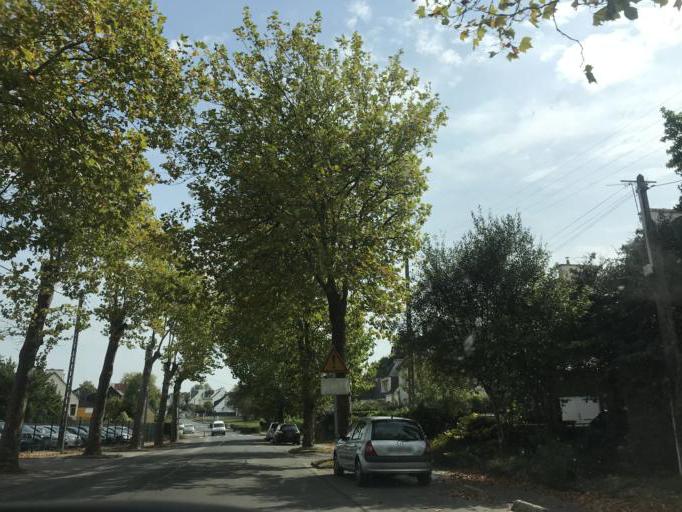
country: FR
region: Brittany
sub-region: Departement du Finistere
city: Le Faou
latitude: 48.2926
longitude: -4.1752
